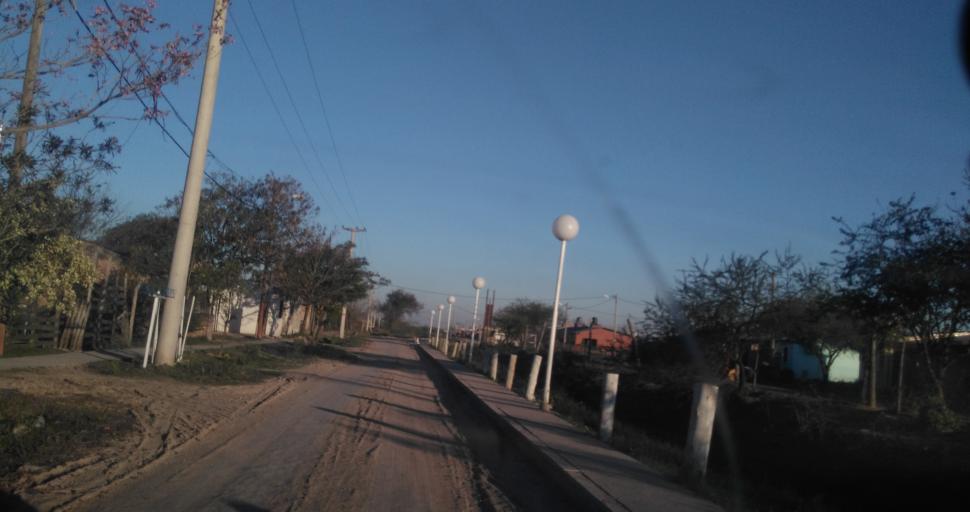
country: AR
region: Chaco
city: Resistencia
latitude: -27.4800
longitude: -59.0113
